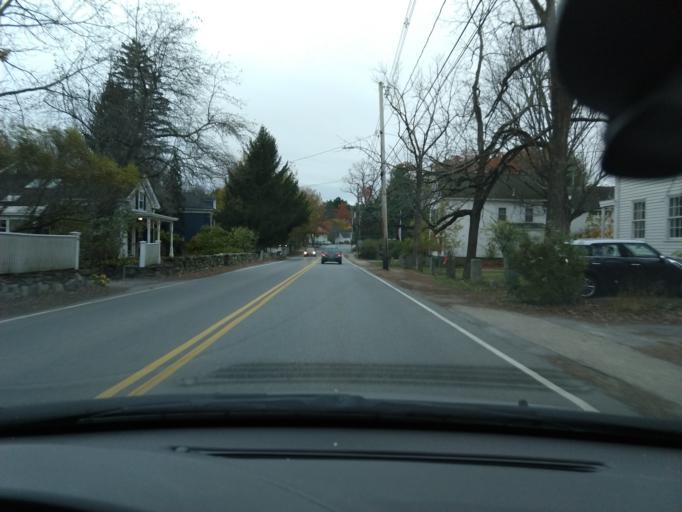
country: US
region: Massachusetts
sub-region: Middlesex County
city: Carlisle
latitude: 42.5312
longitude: -71.3486
